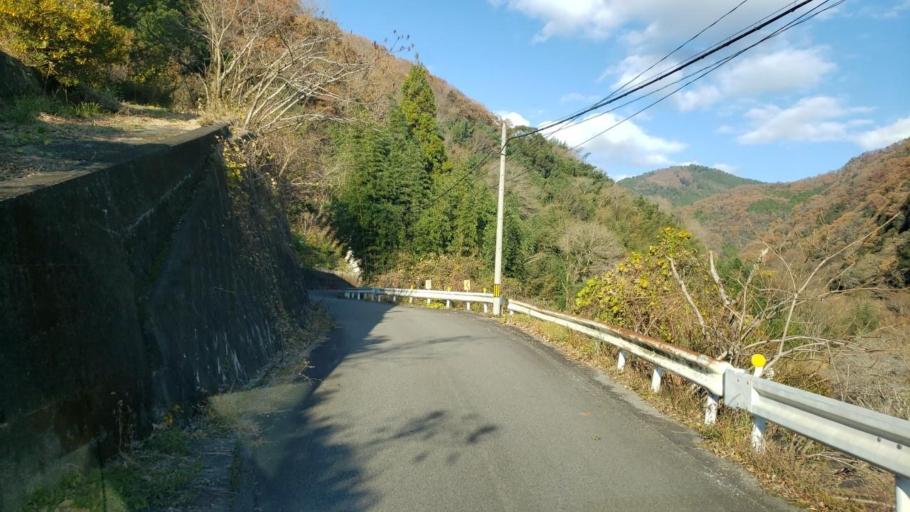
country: JP
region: Tokushima
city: Wakimachi
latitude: 34.0978
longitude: 134.0689
